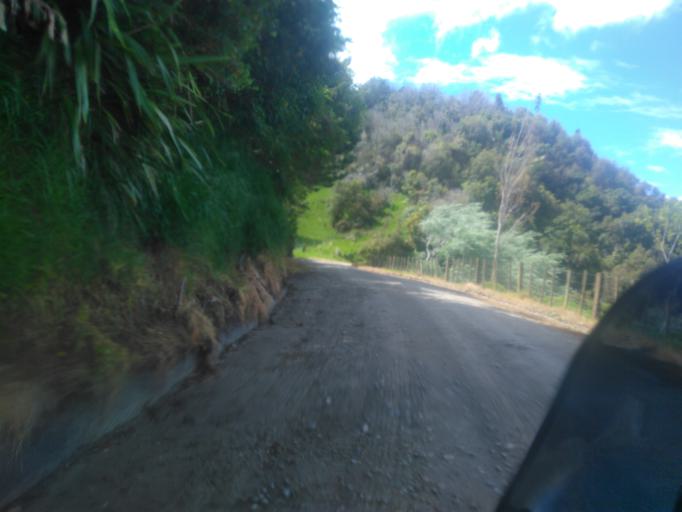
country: NZ
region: Hawke's Bay
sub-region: Wairoa District
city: Wairoa
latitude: -38.7778
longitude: 177.6223
